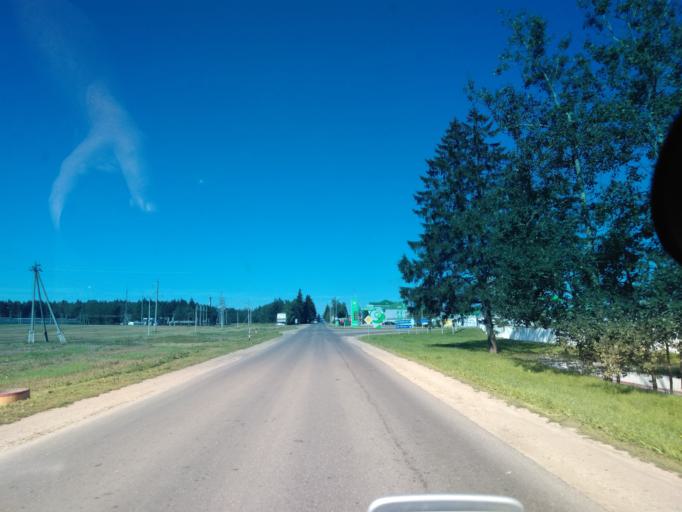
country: BY
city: Fanipol
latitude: 53.7408
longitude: 27.3536
